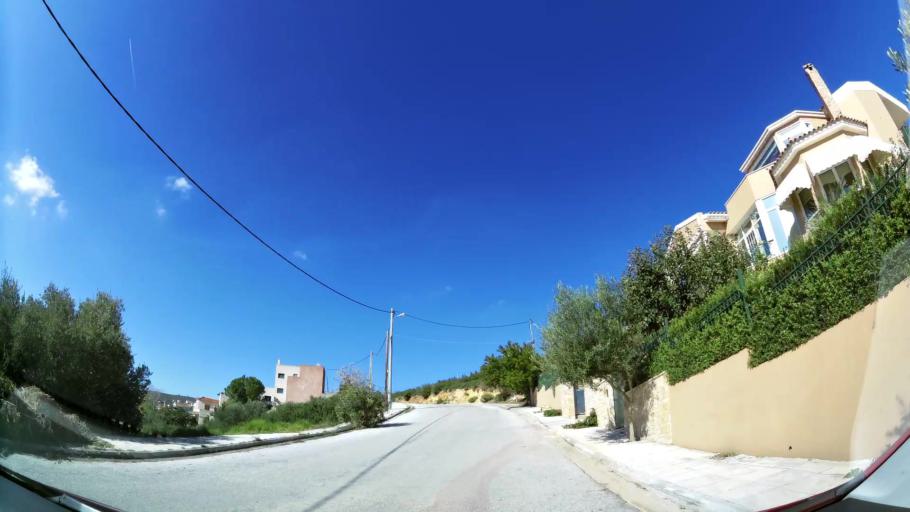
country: GR
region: Attica
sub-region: Nomarchia Anatolikis Attikis
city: Dhrafi
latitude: 38.0079
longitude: 23.9151
